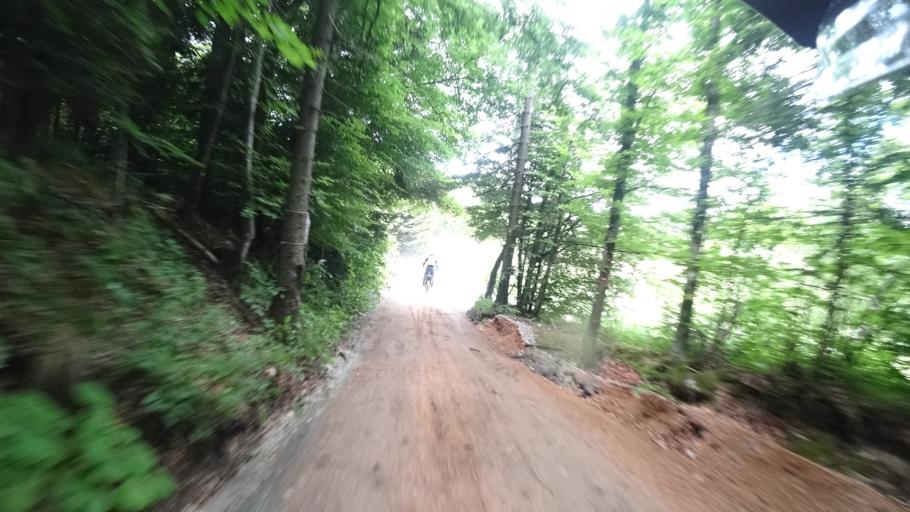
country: HR
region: Primorsko-Goranska
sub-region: Grad Delnice
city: Delnice
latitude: 45.3089
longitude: 14.7433
